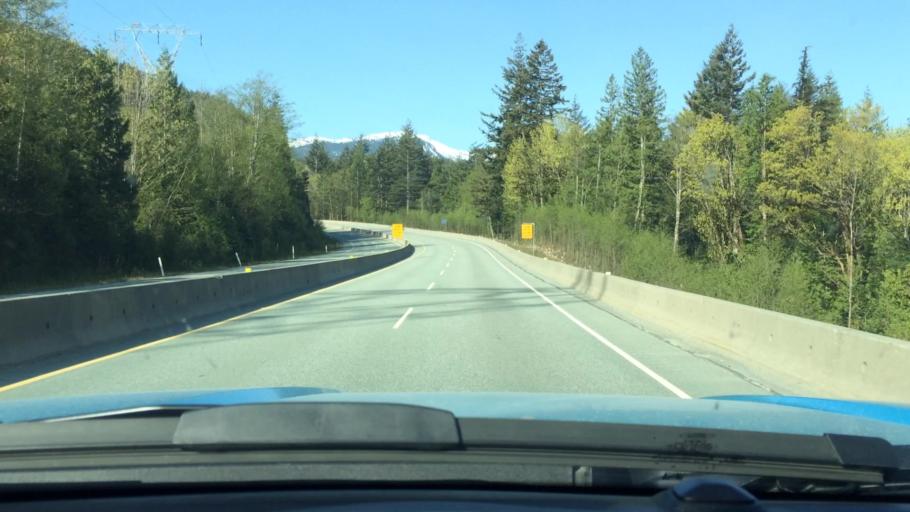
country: CA
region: British Columbia
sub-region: Greater Vancouver Regional District
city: Lions Bay
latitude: 49.6575
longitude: -123.1839
